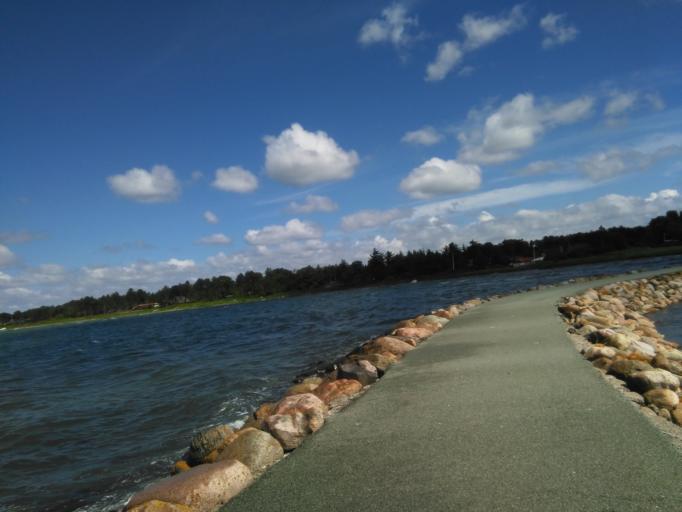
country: DK
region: Central Jutland
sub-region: Arhus Kommune
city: Logten
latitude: 56.1814
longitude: 10.3735
